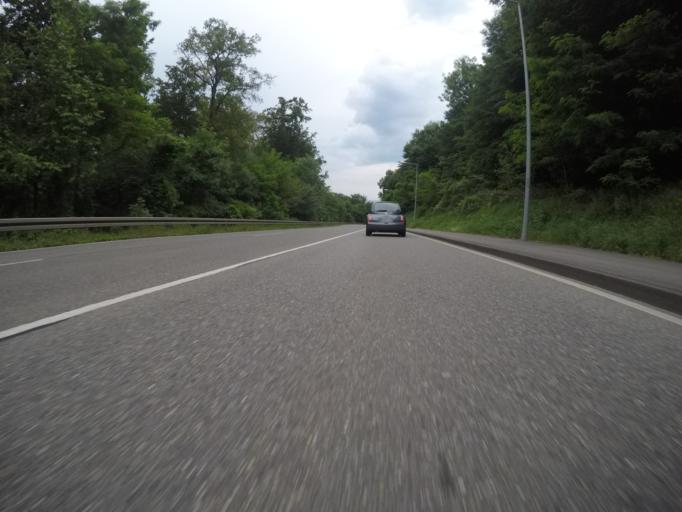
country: DE
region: Baden-Wuerttemberg
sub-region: Regierungsbezirk Stuttgart
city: Stuttgart
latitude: 48.7654
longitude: 9.1378
